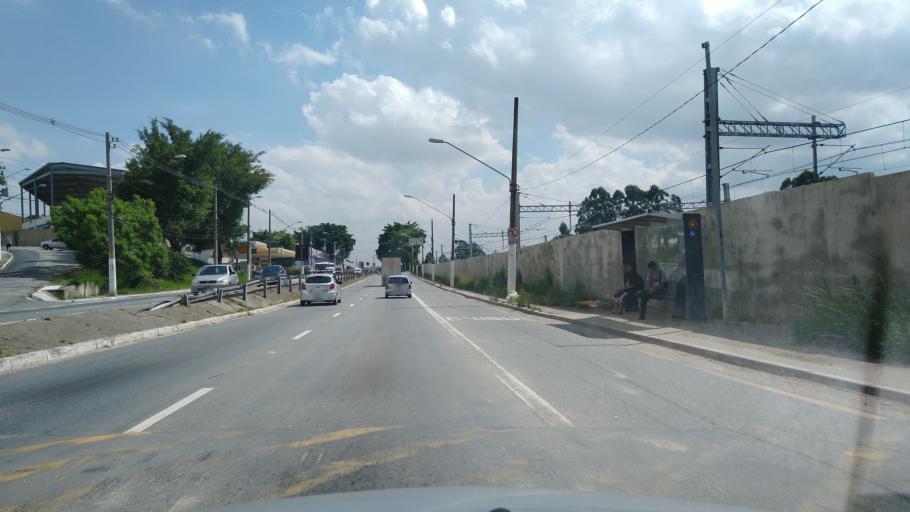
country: BR
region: Sao Paulo
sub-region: Guarulhos
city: Guarulhos
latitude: -23.4961
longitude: -46.5114
